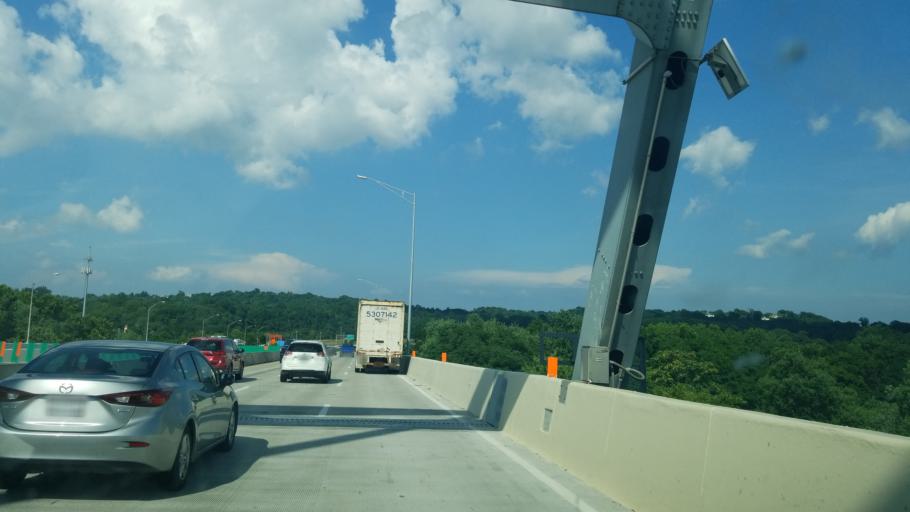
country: US
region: Kentucky
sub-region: Campbell County
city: Fort Thomas
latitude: 39.0579
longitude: -84.4284
